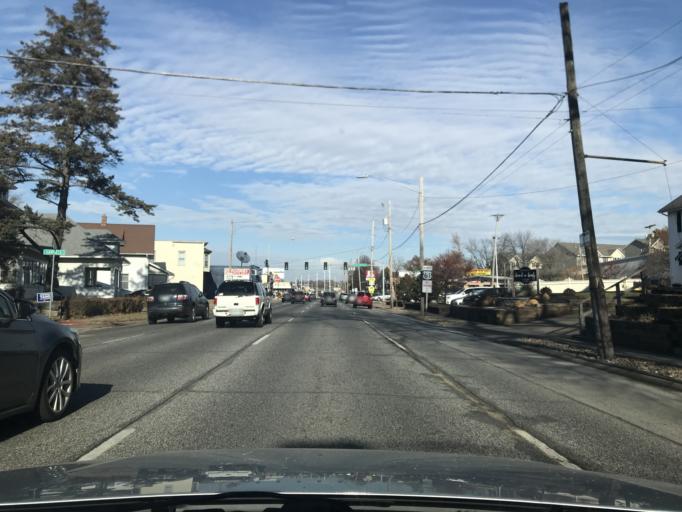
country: US
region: Iowa
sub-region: Scott County
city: Davenport
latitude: 41.5484
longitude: -90.5712
